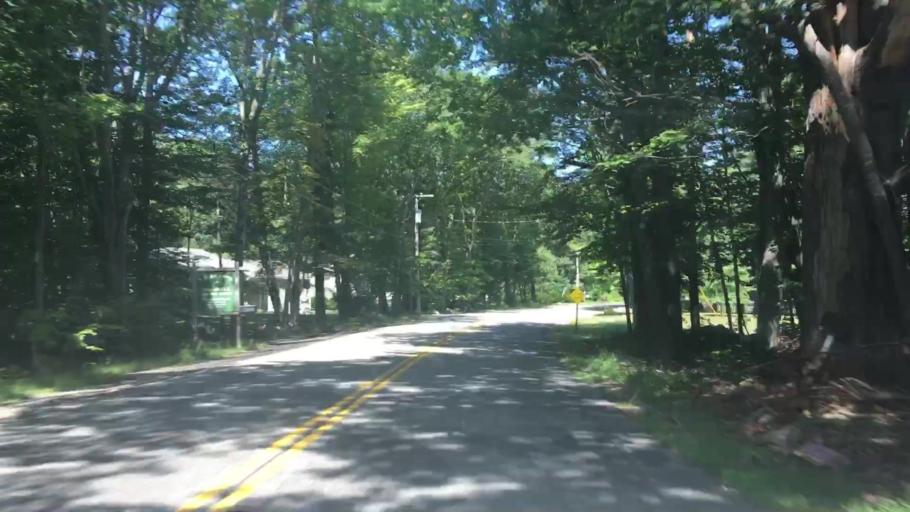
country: US
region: Maine
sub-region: Androscoggin County
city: Lisbon
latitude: 44.0604
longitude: -70.1184
